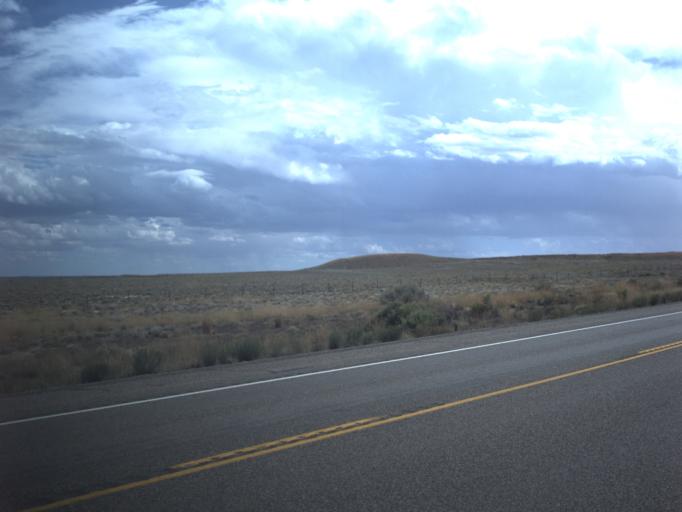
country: US
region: Utah
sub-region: Carbon County
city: Price
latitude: 39.5080
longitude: -110.8352
